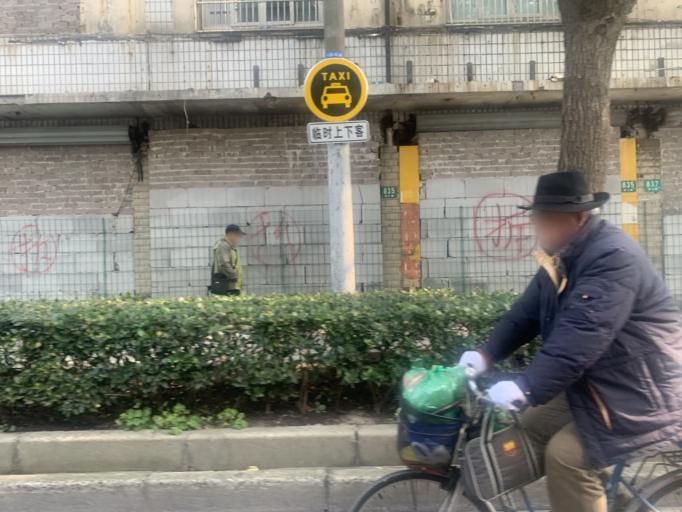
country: CN
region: Shanghai Shi
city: Huamu
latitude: 31.1842
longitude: 121.5151
